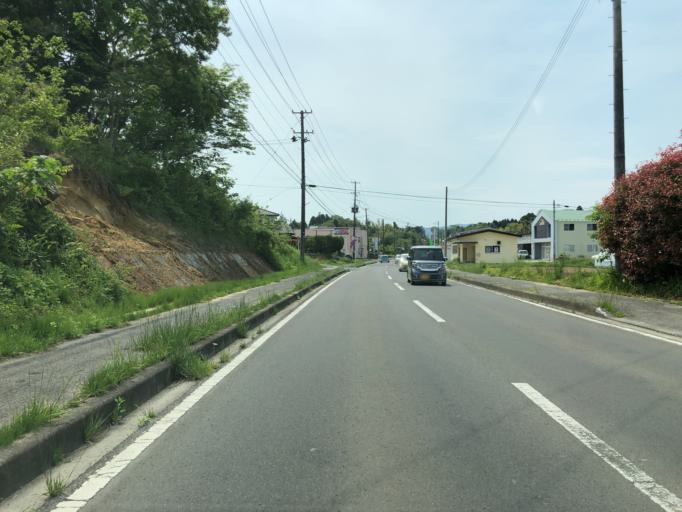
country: JP
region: Miyagi
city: Marumori
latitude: 37.8174
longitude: 140.9353
